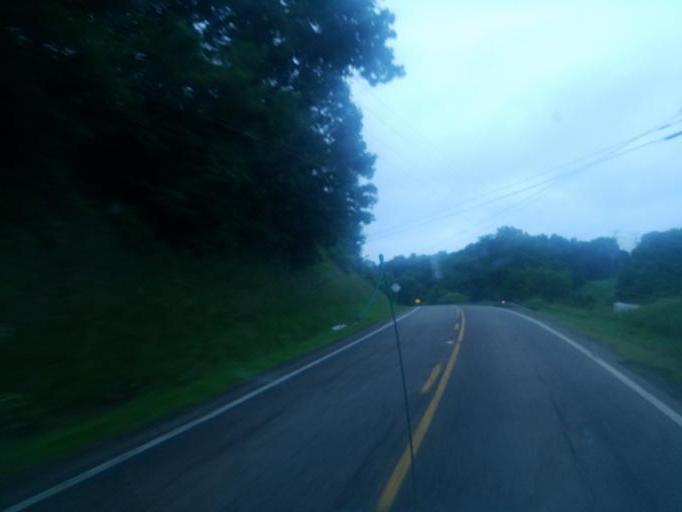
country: US
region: Ohio
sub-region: Carroll County
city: Carrollton
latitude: 40.5725
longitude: -81.0500
